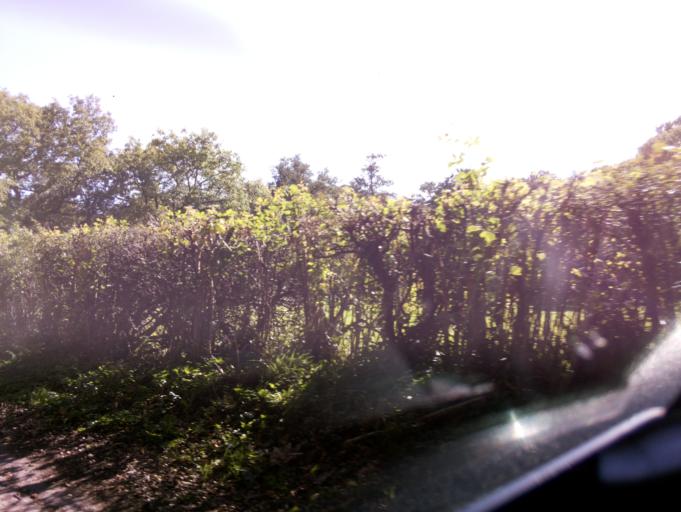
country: GB
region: Wales
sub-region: Torfaen County Borough
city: Cwmbran
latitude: 51.6230
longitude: -3.0410
